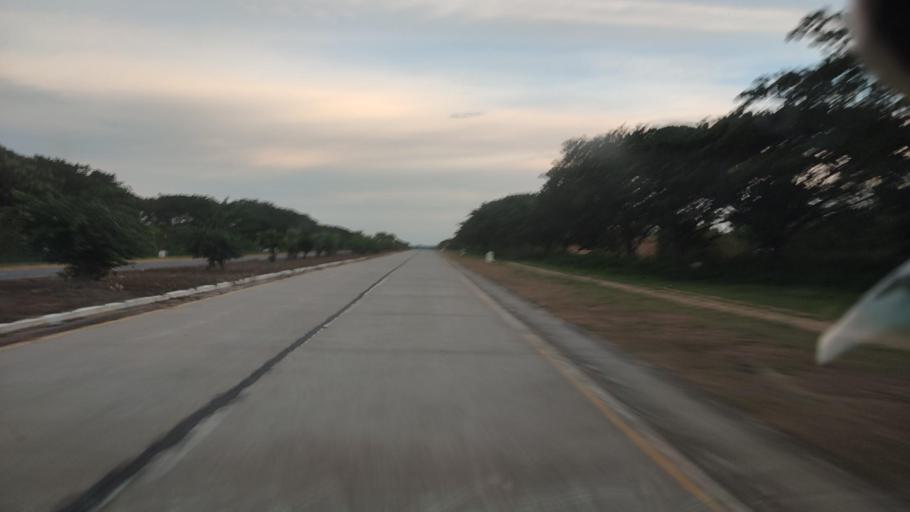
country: MM
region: Mandalay
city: Yamethin
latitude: 20.2834
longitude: 95.8913
